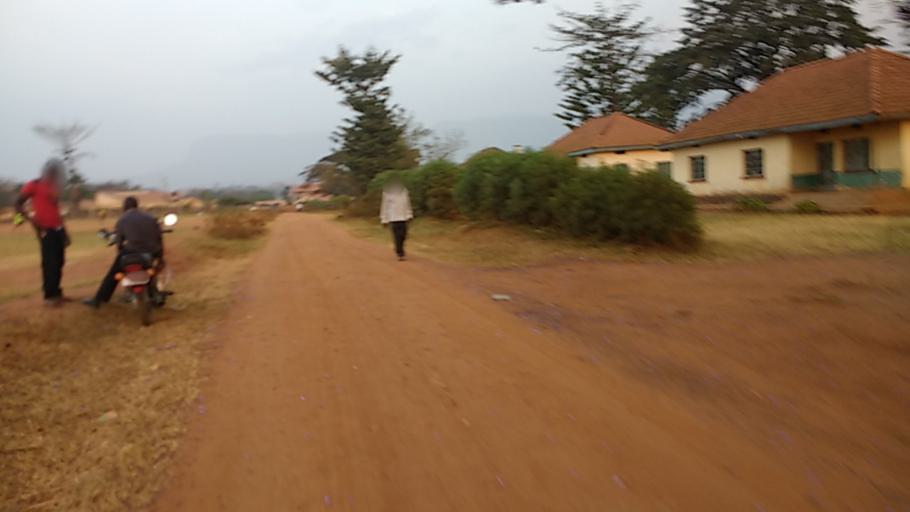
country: UG
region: Eastern Region
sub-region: Mbale District
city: Mbale
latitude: 1.0683
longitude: 34.1680
